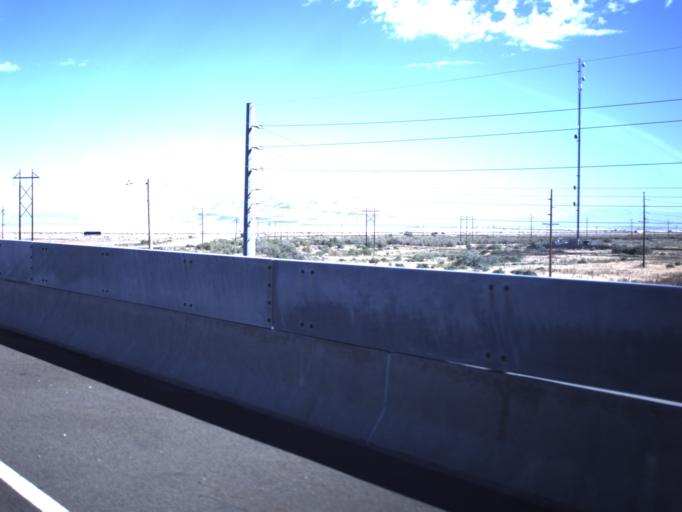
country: US
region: Utah
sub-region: Salt Lake County
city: Magna
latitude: 40.7409
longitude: -112.1778
